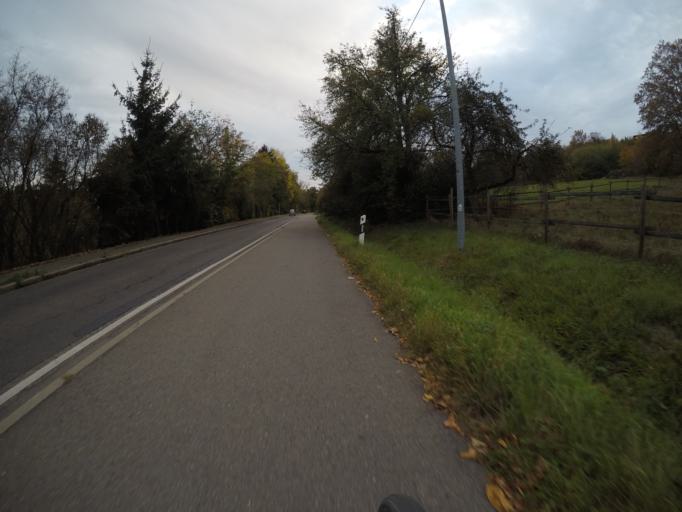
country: DE
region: Baden-Wuerttemberg
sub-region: Regierungsbezirk Stuttgart
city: Leinfelden-Echterdingen
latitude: 48.7366
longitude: 9.1253
